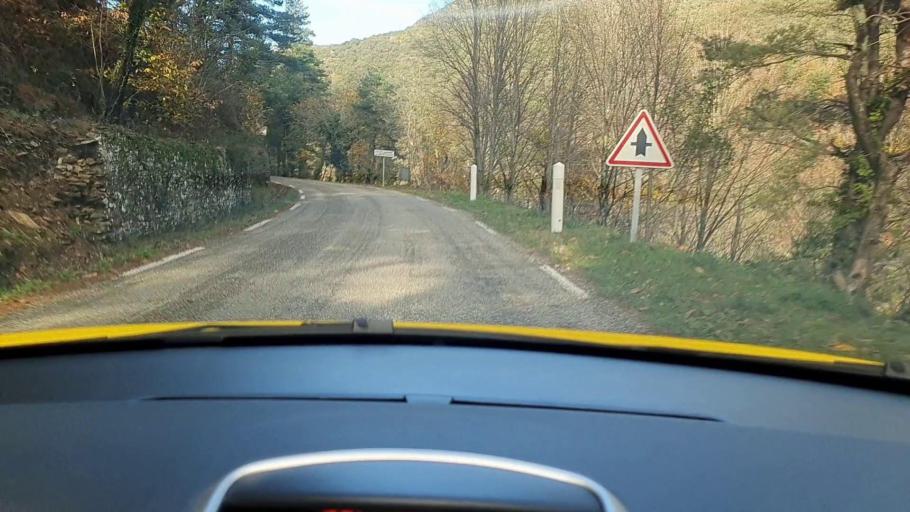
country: FR
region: Languedoc-Roussillon
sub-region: Departement du Gard
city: Valleraugue
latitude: 44.1609
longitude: 3.6737
